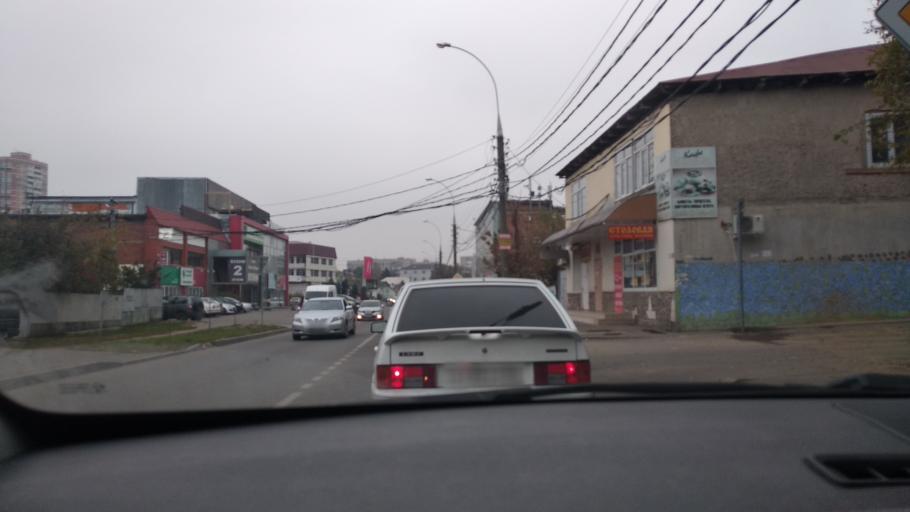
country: RU
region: Krasnodarskiy
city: Krasnodar
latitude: 45.0248
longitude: 39.0082
